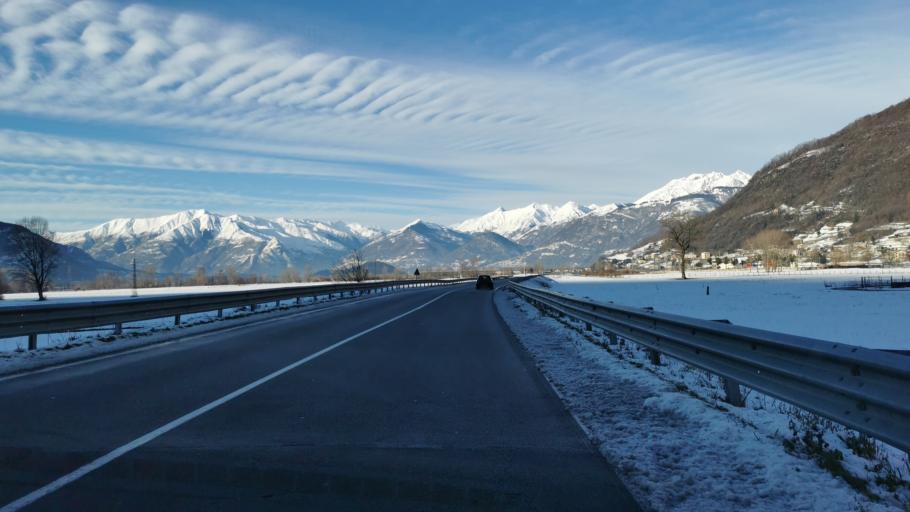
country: IT
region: Lombardy
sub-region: Provincia di Sondrio
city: Delebio
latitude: 46.1504
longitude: 9.4562
